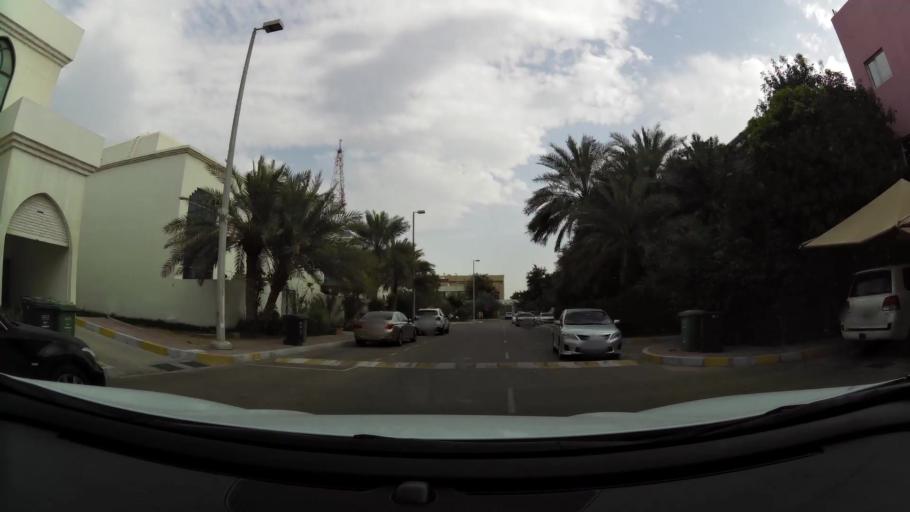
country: AE
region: Abu Dhabi
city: Abu Dhabi
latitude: 24.4613
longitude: 54.3524
